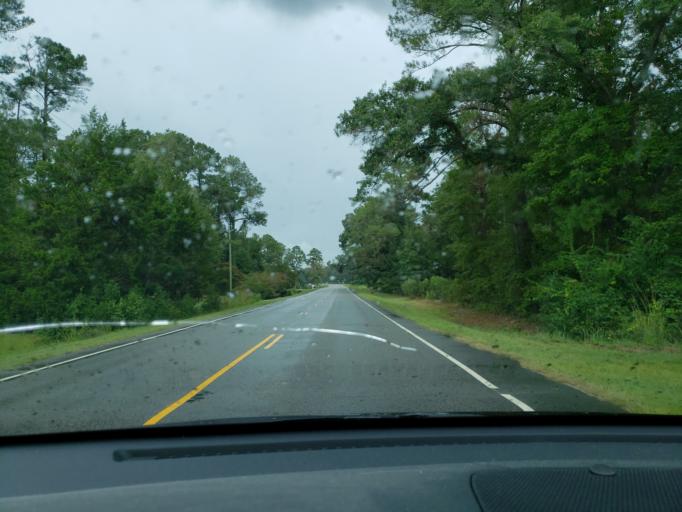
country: US
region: North Carolina
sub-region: Bladen County
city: Elizabethtown
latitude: 34.5088
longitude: -78.6538
